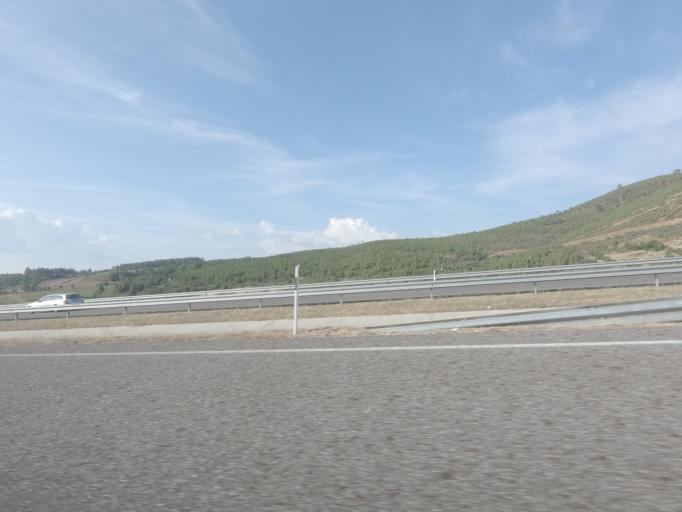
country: ES
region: Galicia
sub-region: Provincia de Ourense
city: Oimbra
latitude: 41.8654
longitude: -7.4300
